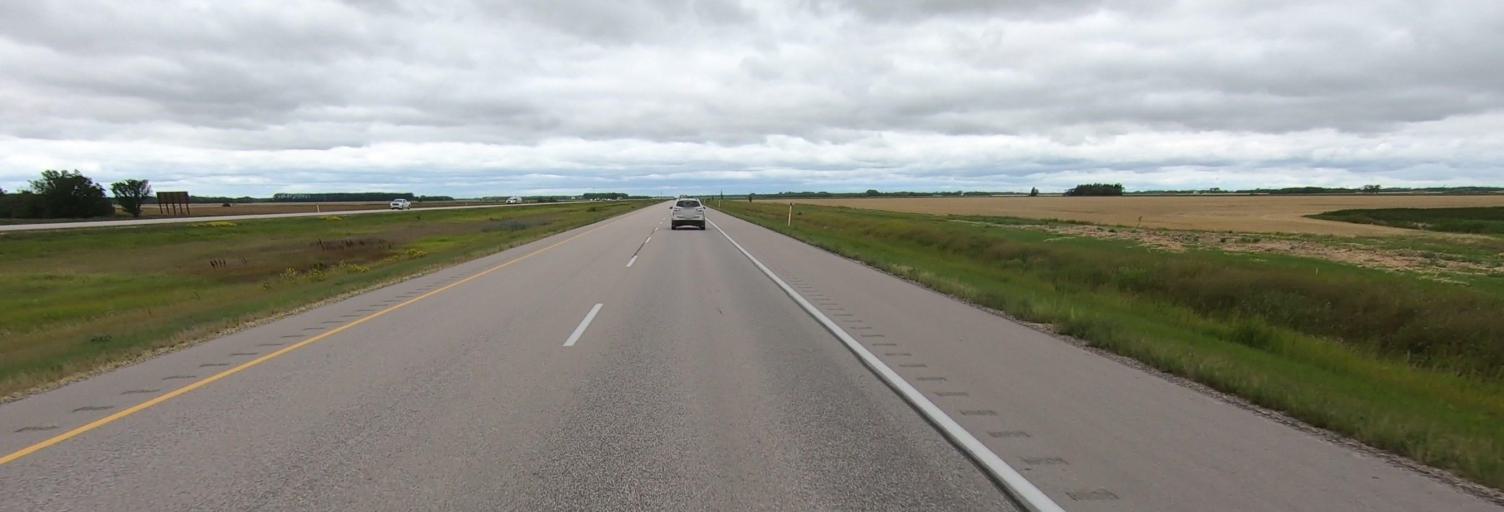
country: CA
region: Manitoba
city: Portage la Prairie
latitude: 49.9386
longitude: -97.9278
